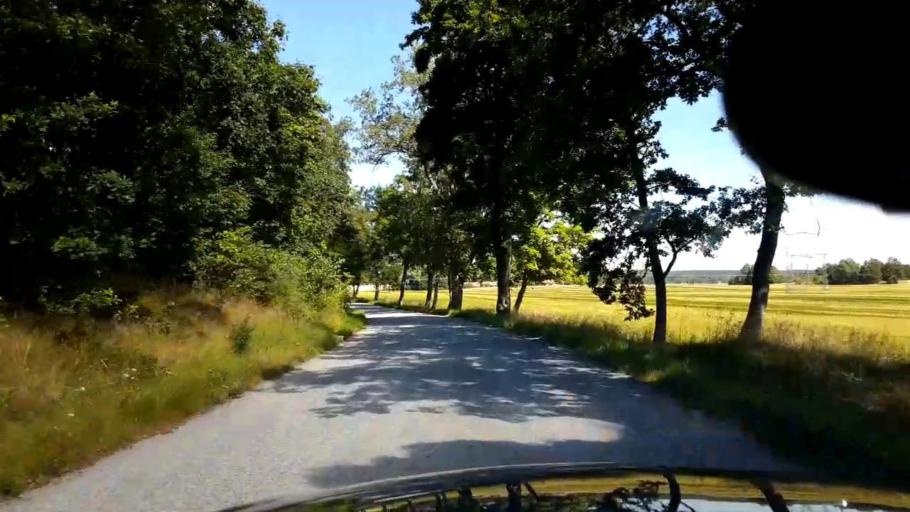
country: SE
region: Stockholm
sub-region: Upplands-Bro Kommun
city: Bro
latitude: 59.5945
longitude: 17.6420
